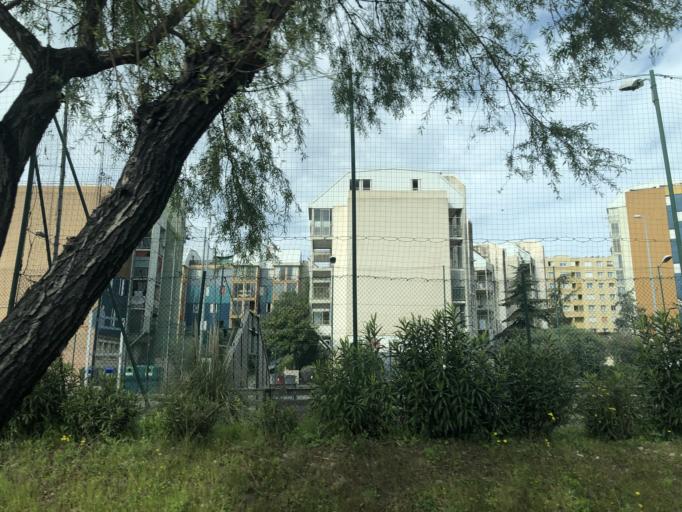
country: FR
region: Provence-Alpes-Cote d'Azur
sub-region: Departement des Alpes-Maritimes
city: Saint-Laurent-du-Var
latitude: 43.6706
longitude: 7.1946
